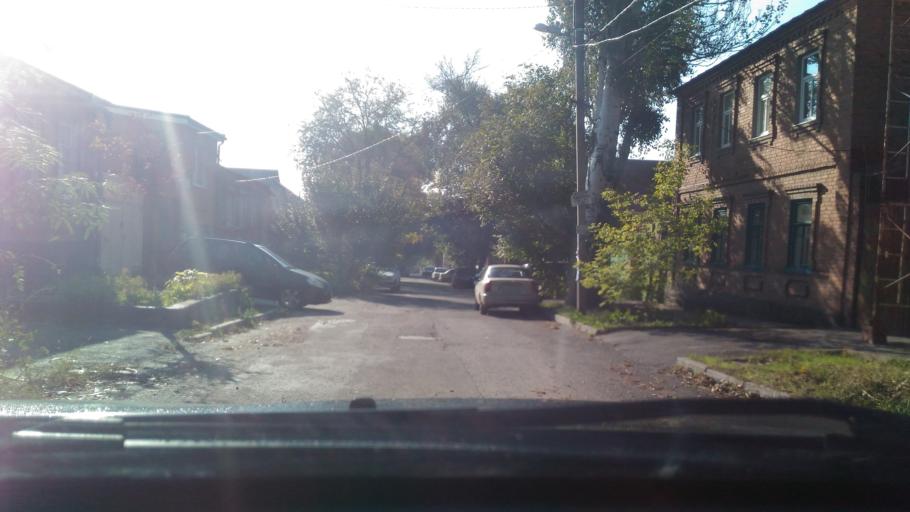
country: RU
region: Rostov
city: Rostov-na-Donu
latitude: 47.2279
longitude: 39.7686
